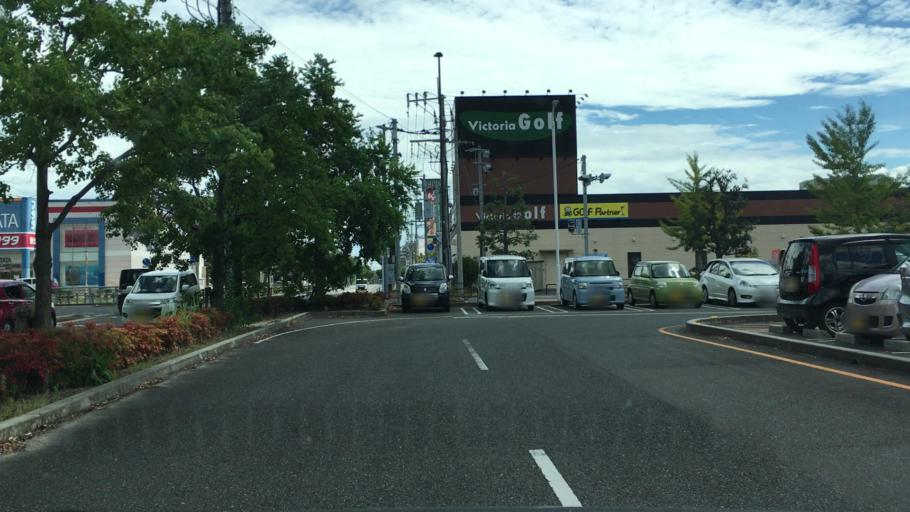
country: JP
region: Saga Prefecture
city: Saga-shi
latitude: 33.2751
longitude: 130.3107
